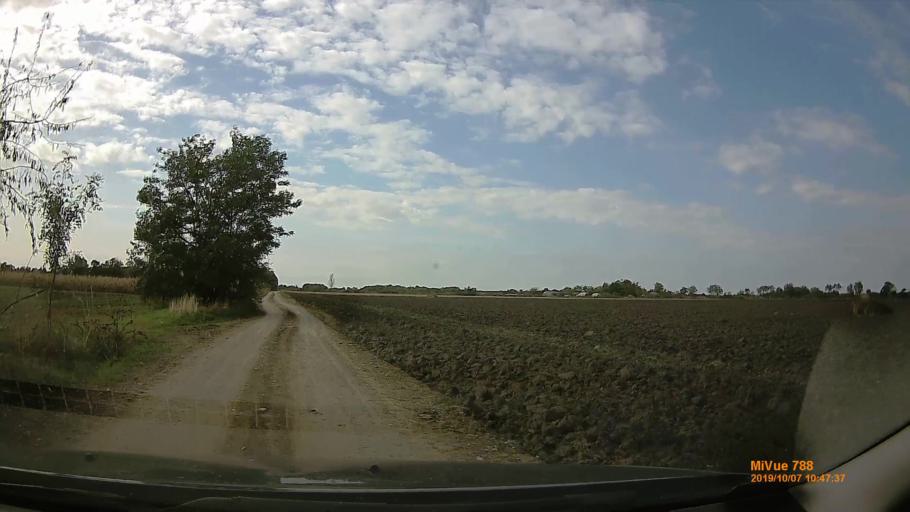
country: HU
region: Bekes
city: Kondoros
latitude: 46.7339
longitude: 20.8146
